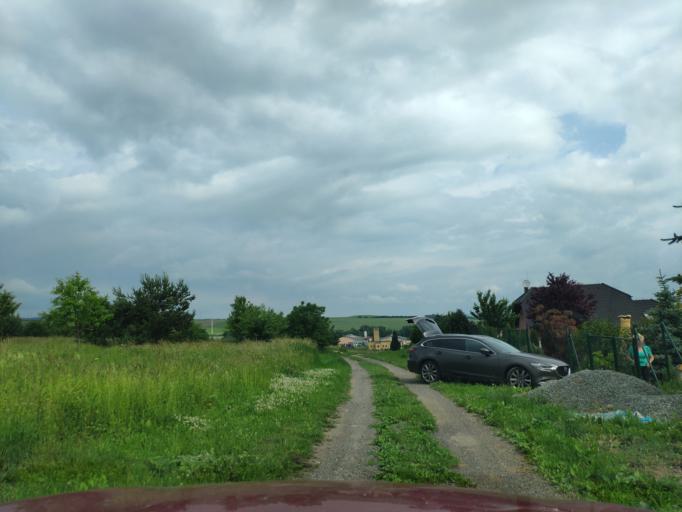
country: SK
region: Kosicky
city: Kosice
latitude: 48.8033
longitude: 21.2985
